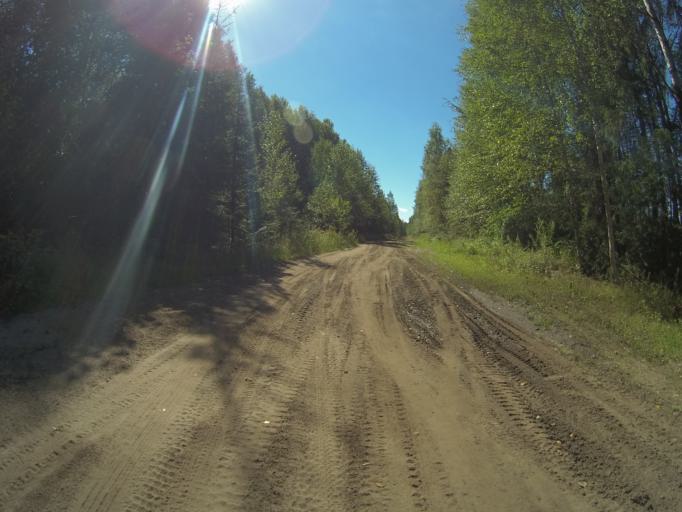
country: RU
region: Vladimir
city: Raduzhnyy
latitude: 55.9378
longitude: 40.2418
